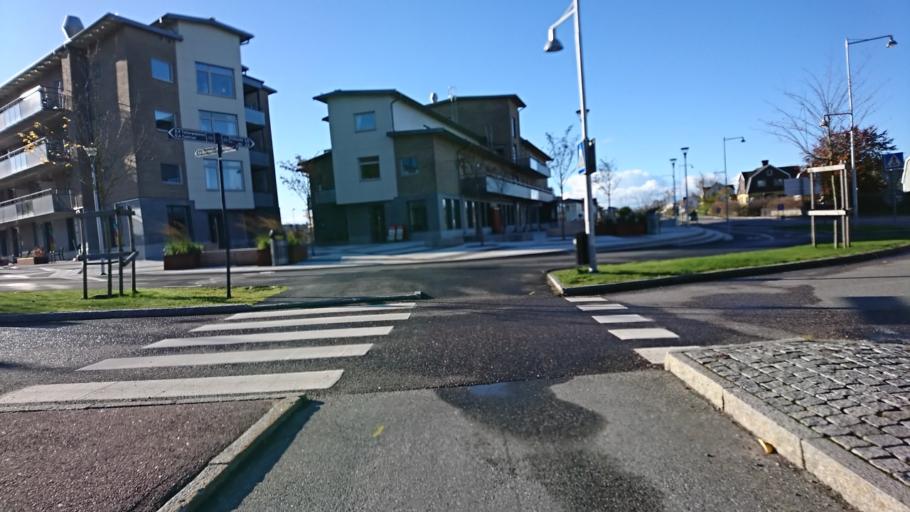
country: SE
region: Vaestra Goetaland
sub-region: Molndal
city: Moelndal
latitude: 57.6543
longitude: 12.0057
